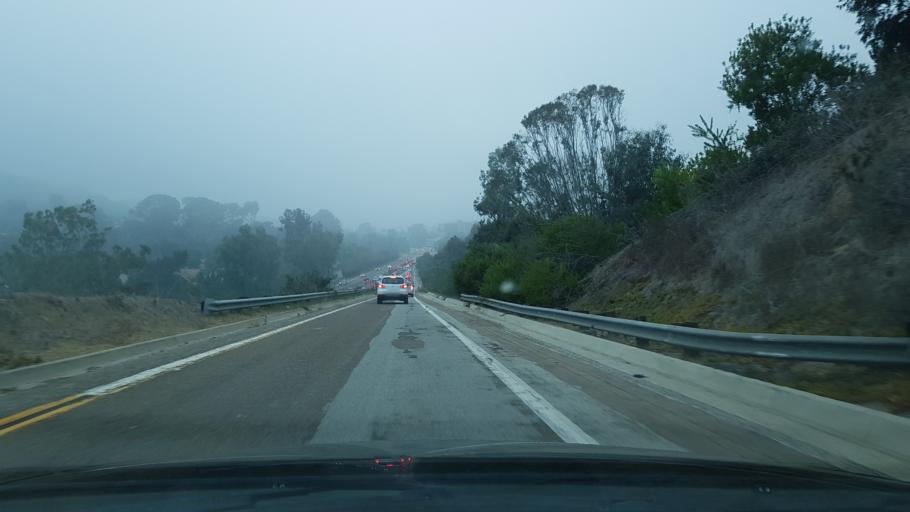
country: US
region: California
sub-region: San Diego County
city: La Jolla
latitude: 32.8473
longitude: -117.2445
